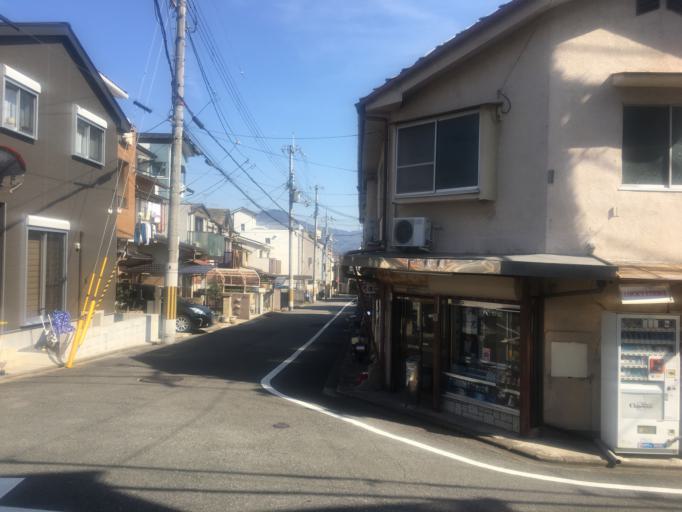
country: JP
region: Kyoto
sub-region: Kyoto-shi
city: Kamigyo-ku
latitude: 35.0537
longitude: 135.7454
